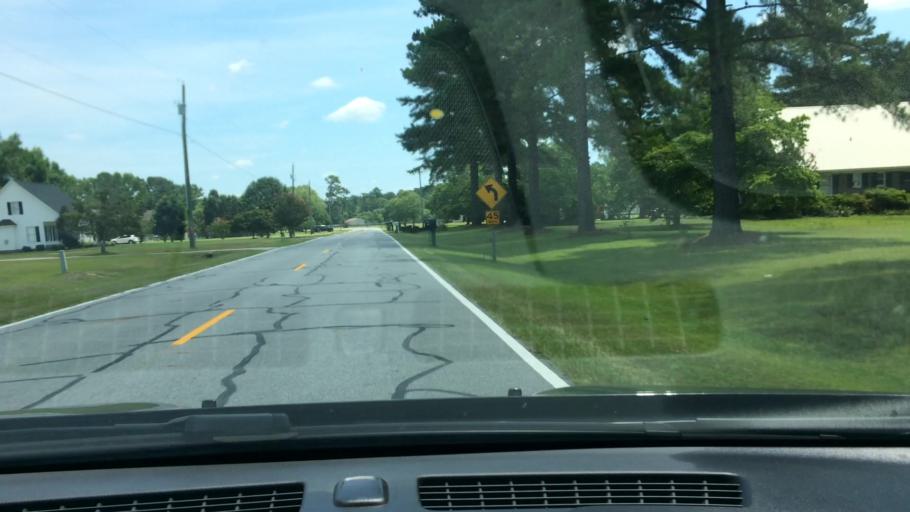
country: US
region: North Carolina
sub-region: Pitt County
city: Windsor
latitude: 35.4980
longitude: -77.3390
